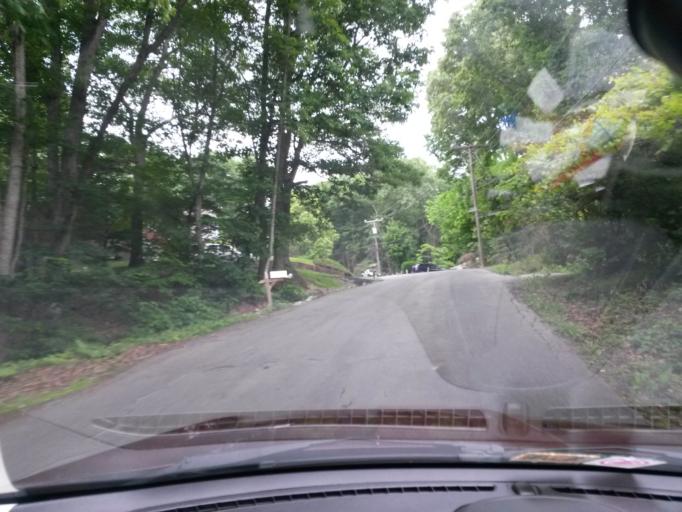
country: US
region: Virginia
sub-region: City of Covington
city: Fairlawn
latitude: 37.7816
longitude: -79.9188
